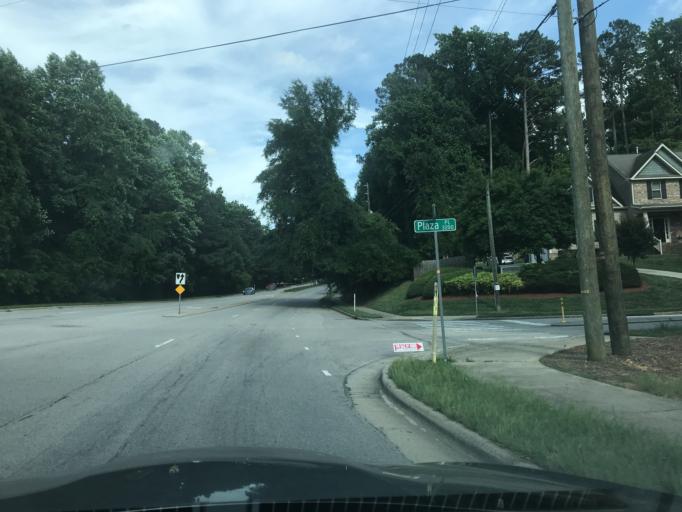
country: US
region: North Carolina
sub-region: Wake County
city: West Raleigh
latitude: 35.8613
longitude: -78.6871
